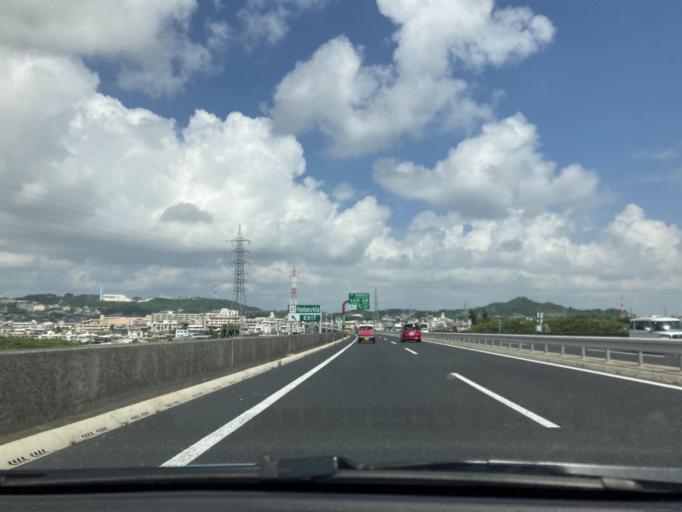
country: JP
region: Okinawa
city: Tomigusuku
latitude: 26.1924
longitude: 127.7391
